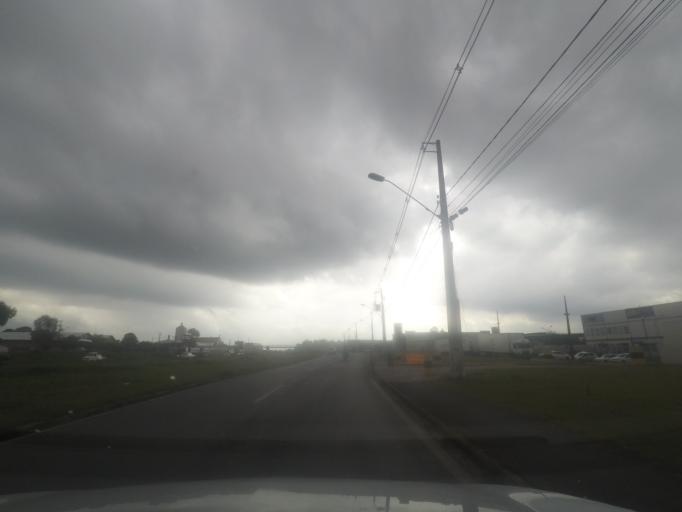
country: BR
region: Parana
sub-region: Sao Jose Dos Pinhais
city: Sao Jose dos Pinhais
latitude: -25.5489
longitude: -49.2839
